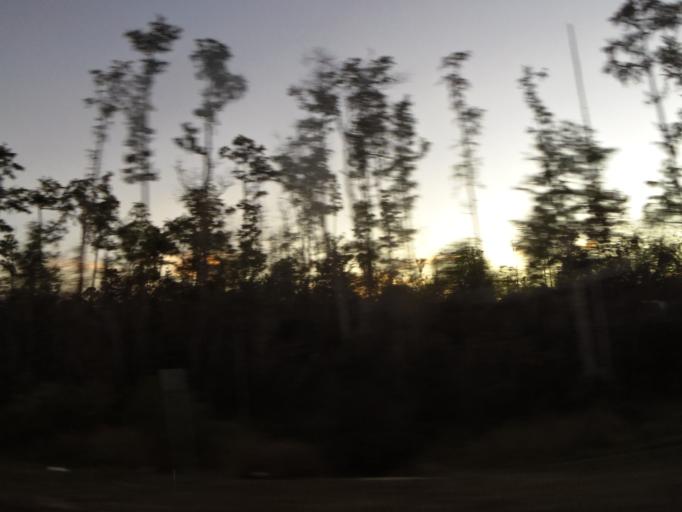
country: US
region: Florida
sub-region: Flagler County
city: Palm Coast
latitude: 29.6016
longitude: -81.2472
